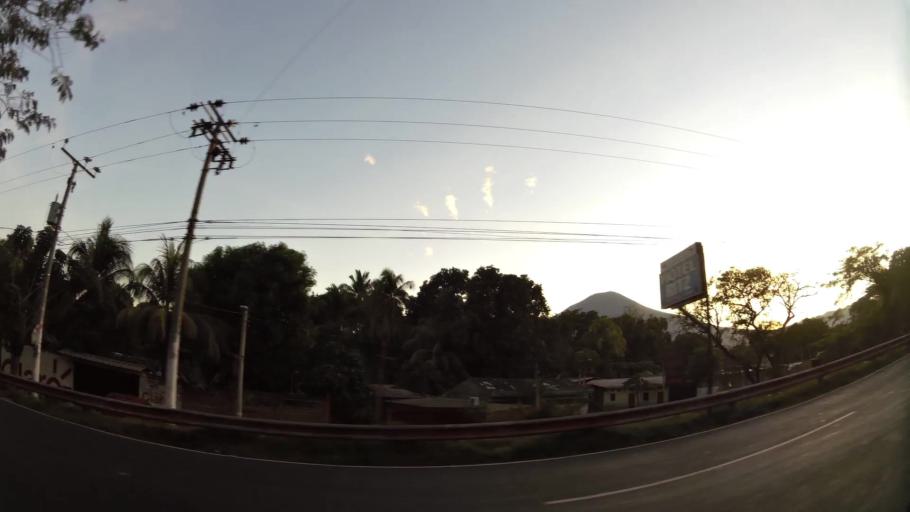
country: SV
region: San Miguel
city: San Miguel
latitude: 13.4989
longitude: -88.2090
